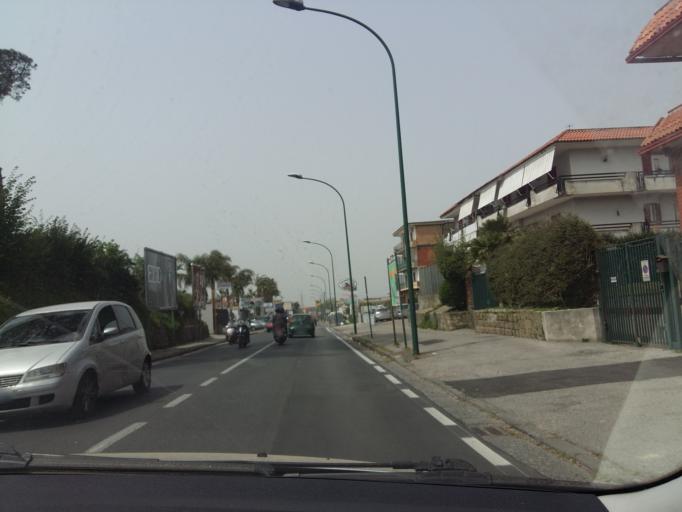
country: IT
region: Campania
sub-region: Provincia di Napoli
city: Mugnano di Napoli
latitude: 40.8947
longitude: 14.2162
